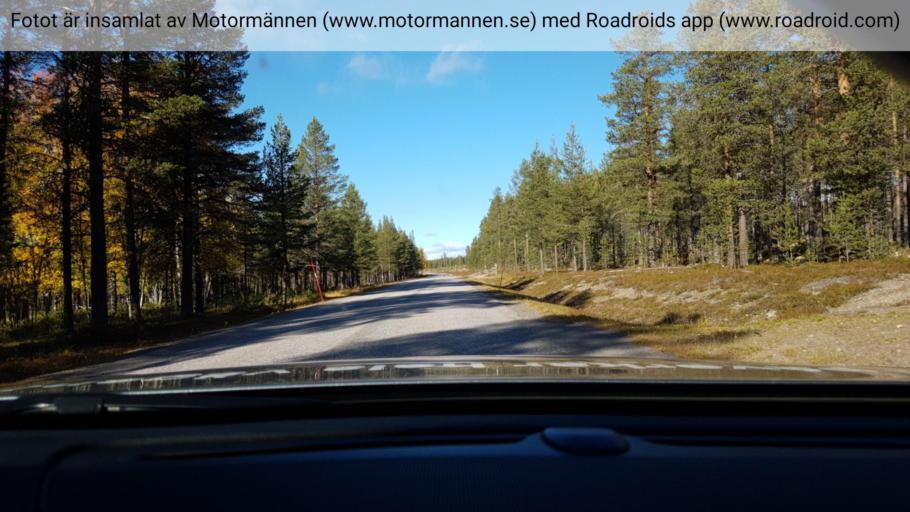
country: SE
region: Vaesterbotten
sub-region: Mala Kommun
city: Mala
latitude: 65.7688
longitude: 18.5399
